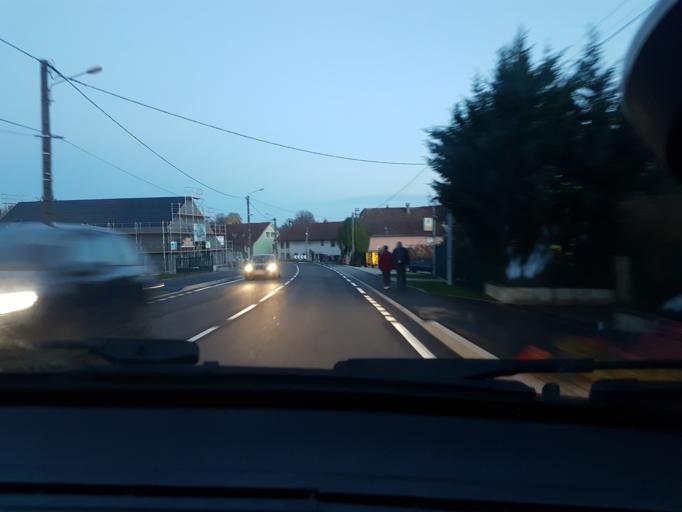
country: FR
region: Franche-Comte
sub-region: Territoire de Belfort
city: Essert
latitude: 47.6351
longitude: 6.8089
